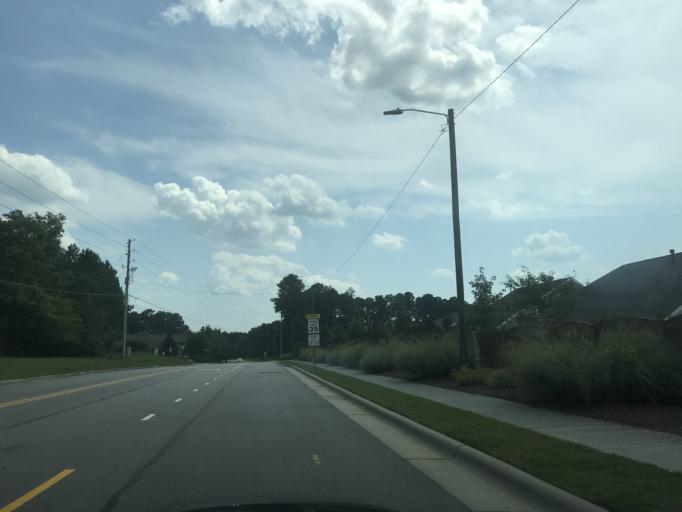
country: US
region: North Carolina
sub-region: Wake County
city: West Raleigh
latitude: 35.8942
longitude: -78.6536
